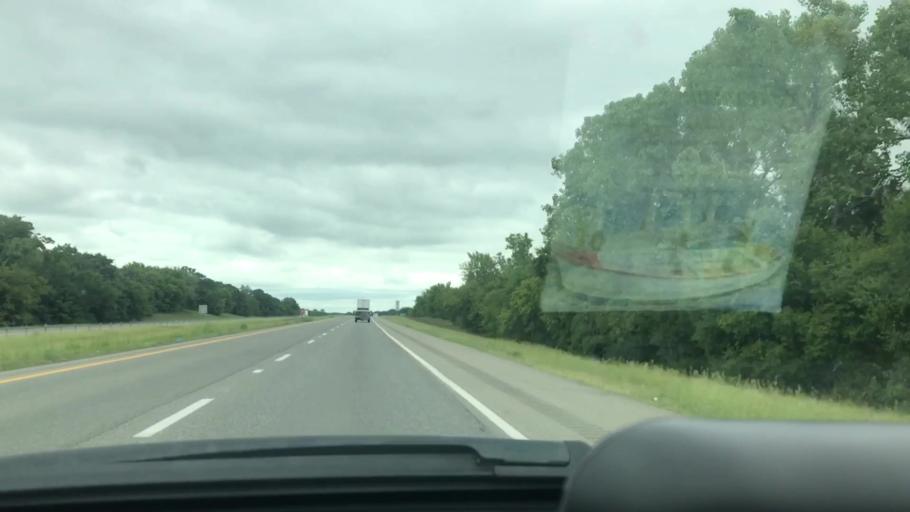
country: US
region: Oklahoma
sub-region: McIntosh County
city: Eufaula
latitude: 35.3699
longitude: -95.5716
